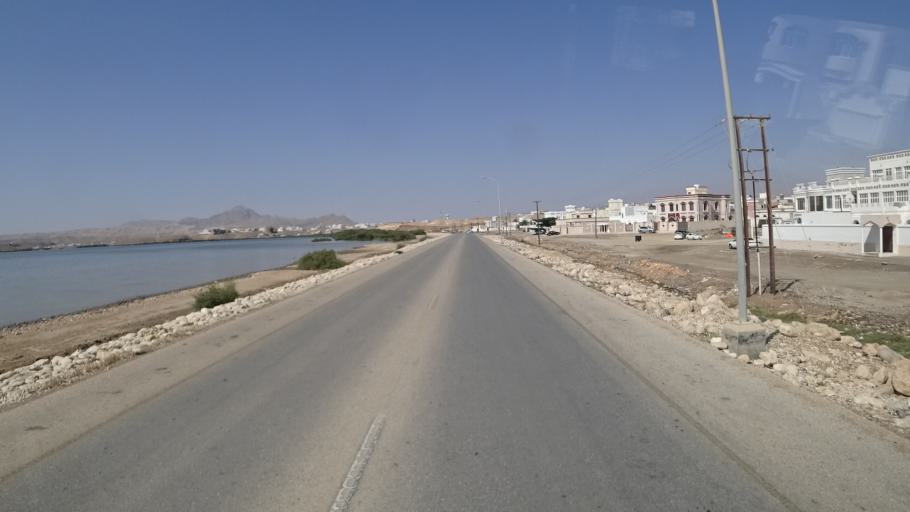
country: OM
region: Ash Sharqiyah
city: Sur
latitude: 22.5694
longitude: 59.5143
